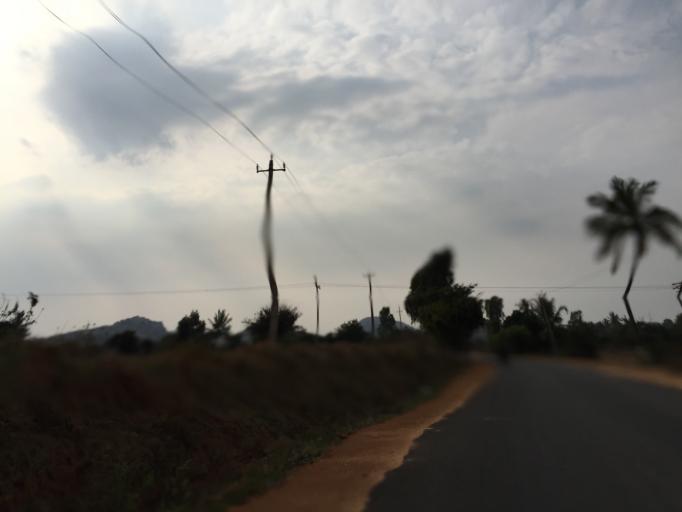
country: IN
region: Karnataka
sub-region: Chikkaballapur
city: Gudibanda
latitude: 13.5716
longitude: 77.7287
